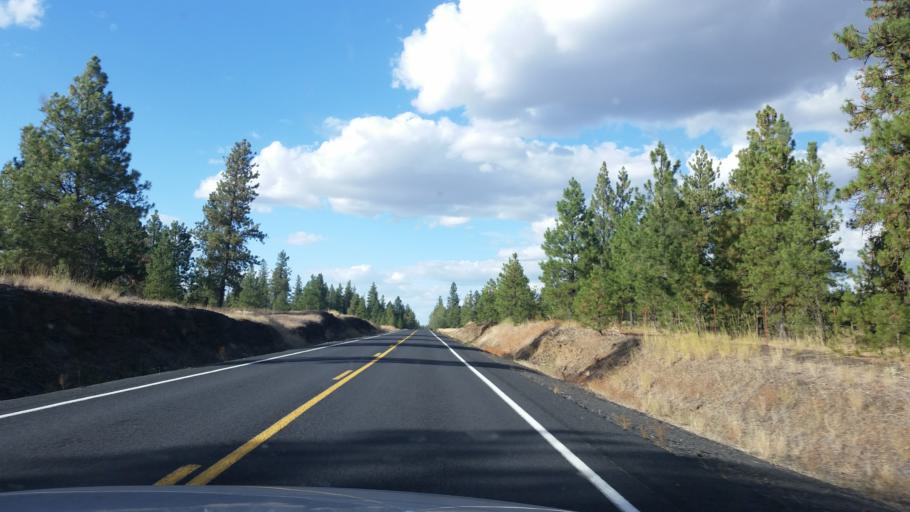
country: US
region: Washington
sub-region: Spokane County
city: Cheney
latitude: 47.4055
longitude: -117.5701
